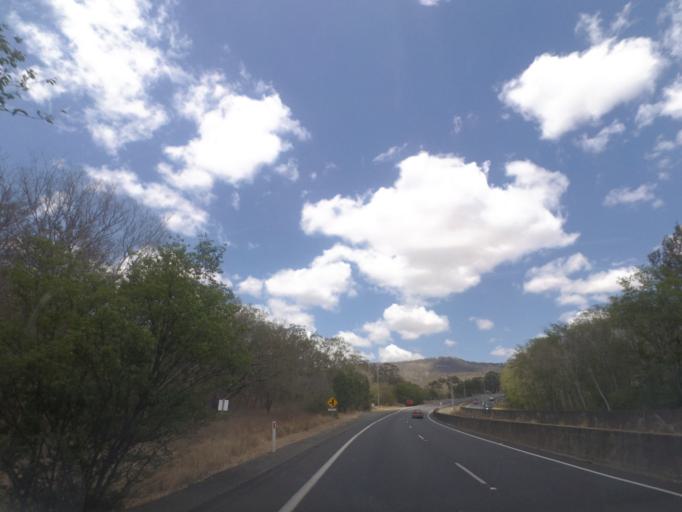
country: AU
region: Queensland
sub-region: Toowoomba
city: East Toowoomba
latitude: -27.5610
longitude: 152.0060
